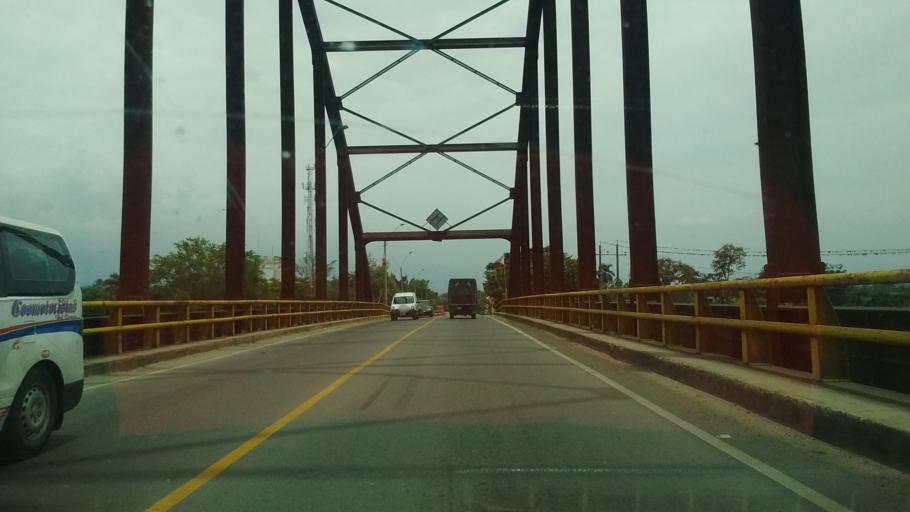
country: CO
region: Valle del Cauca
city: Jamundi
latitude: 3.3017
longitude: -76.4770
